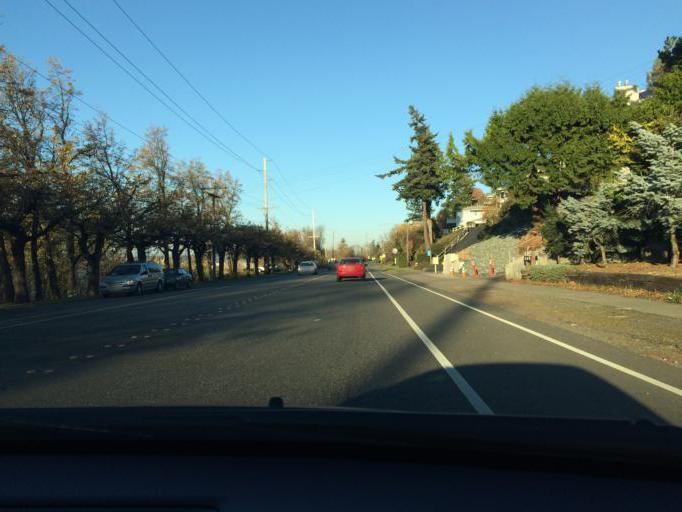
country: US
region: Washington
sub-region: Whatcom County
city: Bellingham
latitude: 48.7336
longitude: -122.4981
